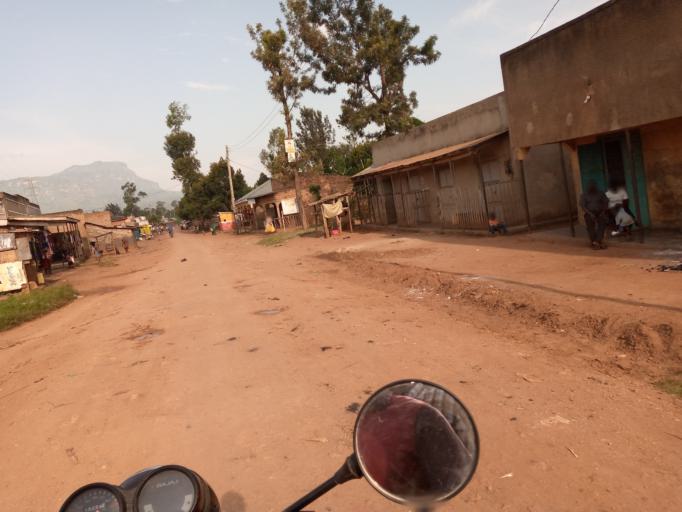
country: UG
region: Eastern Region
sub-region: Mbale District
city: Mbale
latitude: 1.0572
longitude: 34.1592
